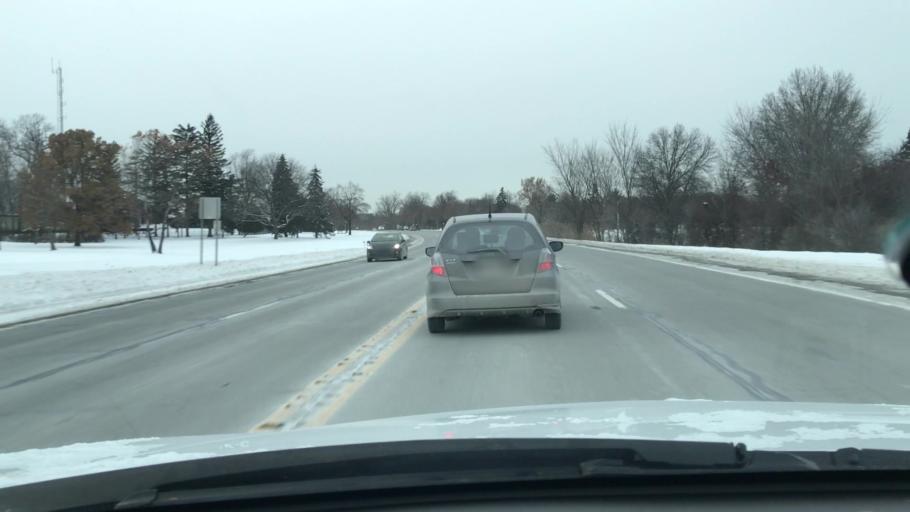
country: US
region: Michigan
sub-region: Oakland County
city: Pontiac
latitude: 42.6534
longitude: -83.3282
